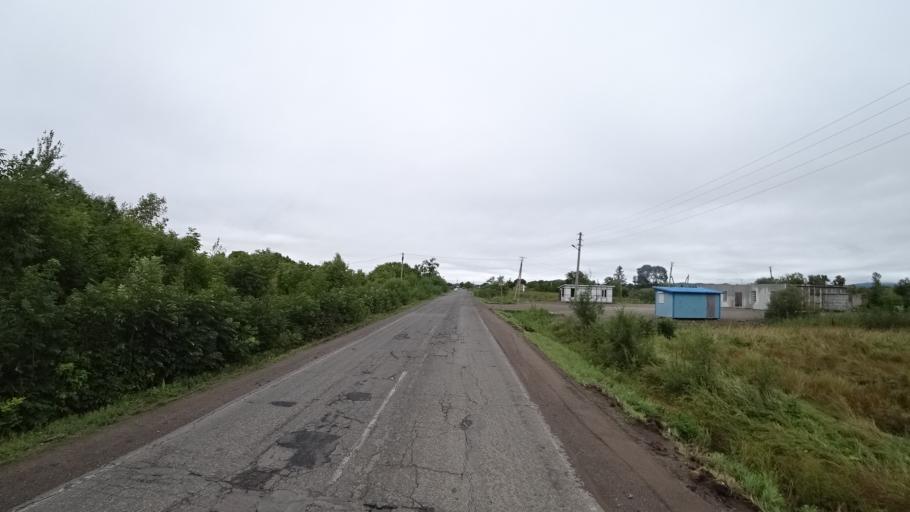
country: RU
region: Primorskiy
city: Monastyrishche
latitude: 44.1912
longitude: 132.4812
